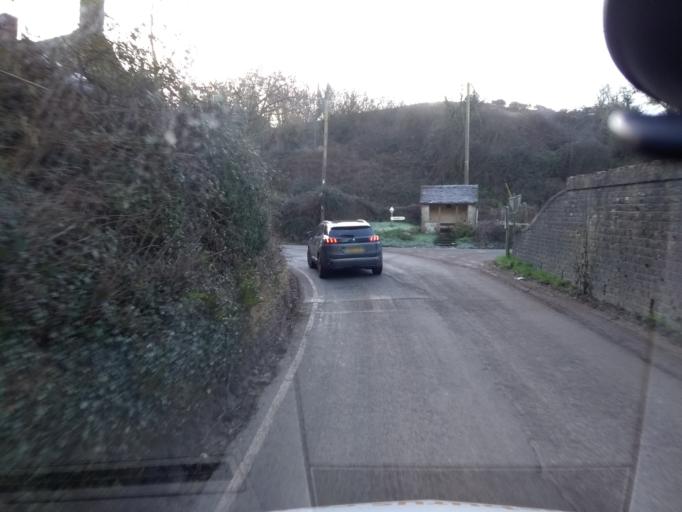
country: GB
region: England
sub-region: Somerset
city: Evercreech
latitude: 51.1324
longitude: -2.4780
